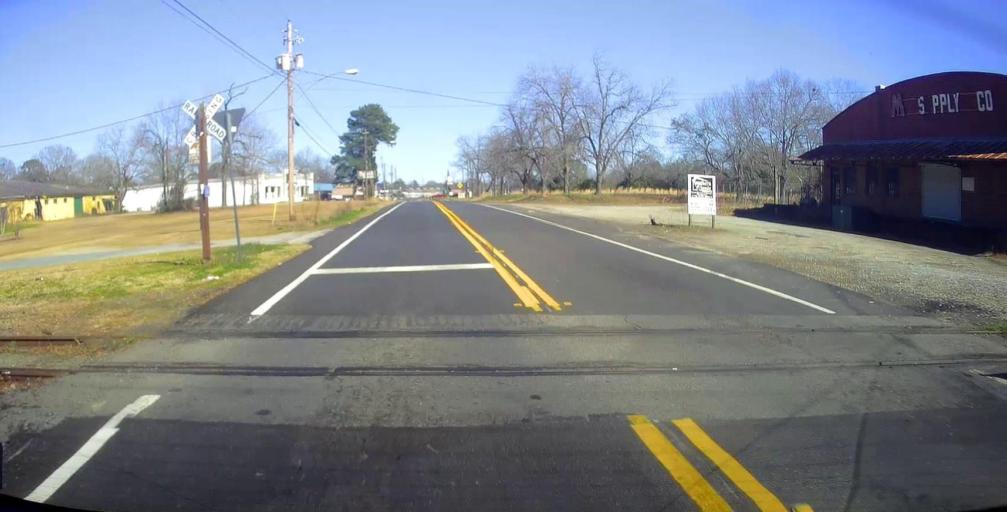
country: US
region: Georgia
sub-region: Peach County
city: Fort Valley
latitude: 32.5486
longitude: -83.8925
